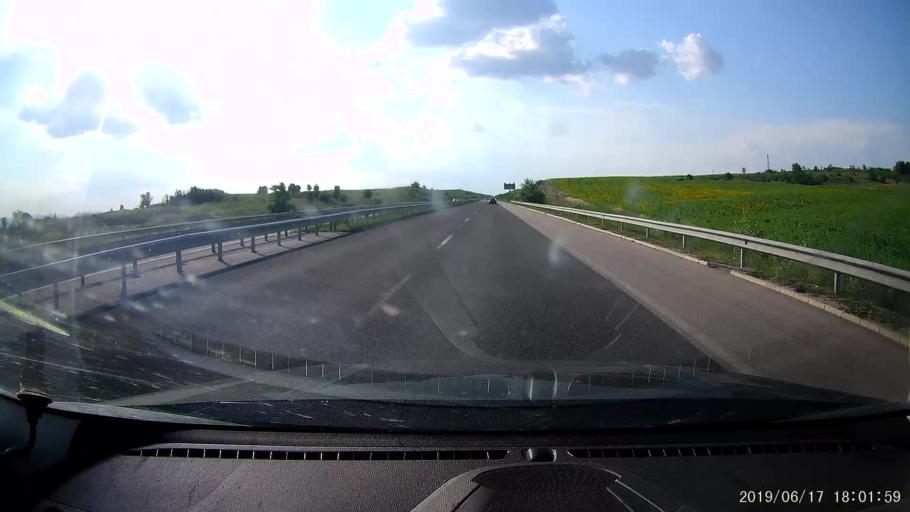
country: BG
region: Khaskovo
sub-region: Obshtina Svilengrad
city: Svilengrad
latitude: 41.7517
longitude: 26.2399
